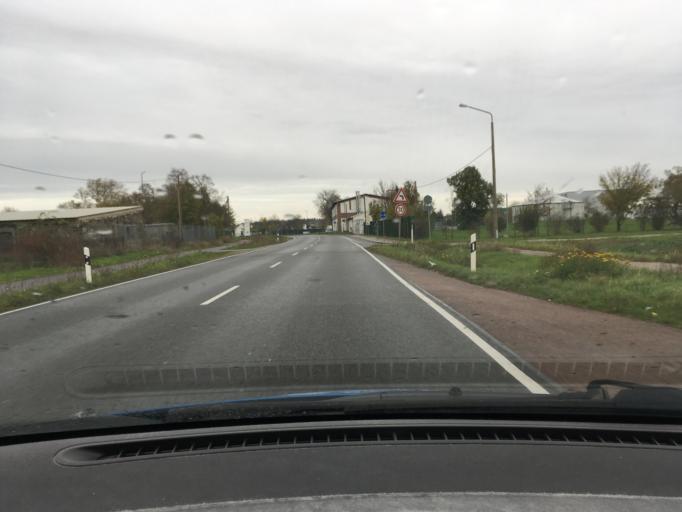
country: DE
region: Saxony-Anhalt
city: Rodleben
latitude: 51.8997
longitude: 12.2155
